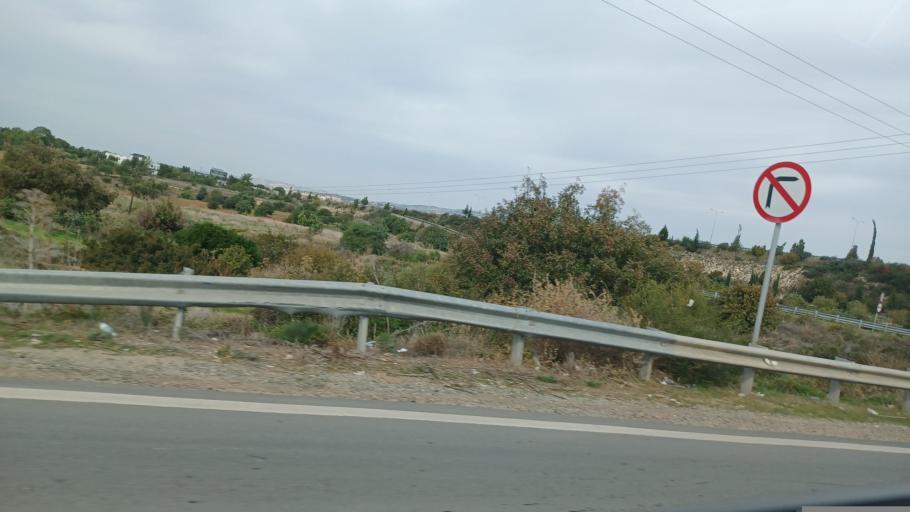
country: CY
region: Pafos
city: Paphos
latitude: 34.7742
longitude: 32.4590
